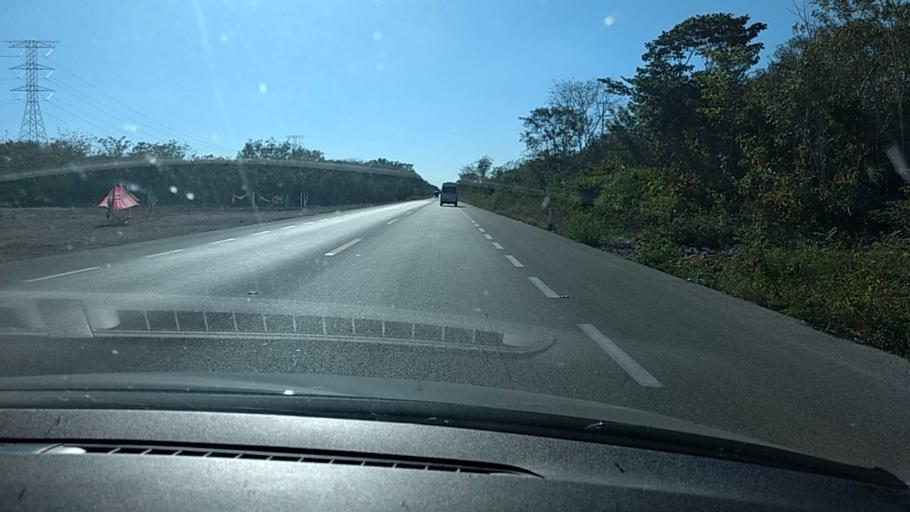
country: MX
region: Yucatan
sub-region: Uayma
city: Uayma
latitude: 20.6285
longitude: -88.3751
